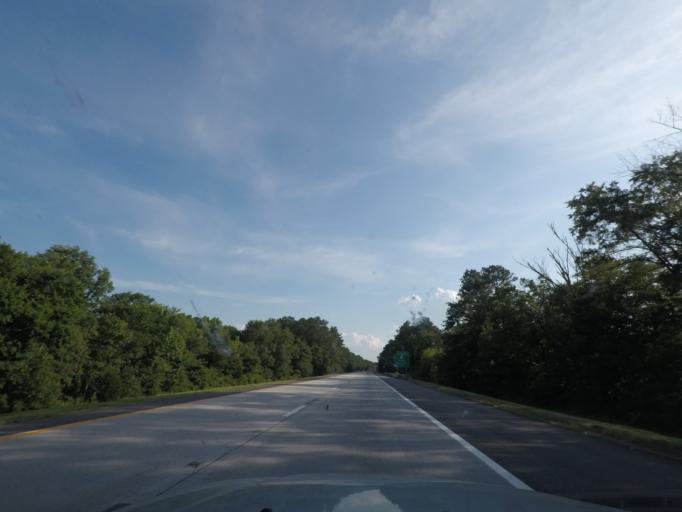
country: US
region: North Carolina
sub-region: Granville County
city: Creedmoor
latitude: 36.1628
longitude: -78.7124
